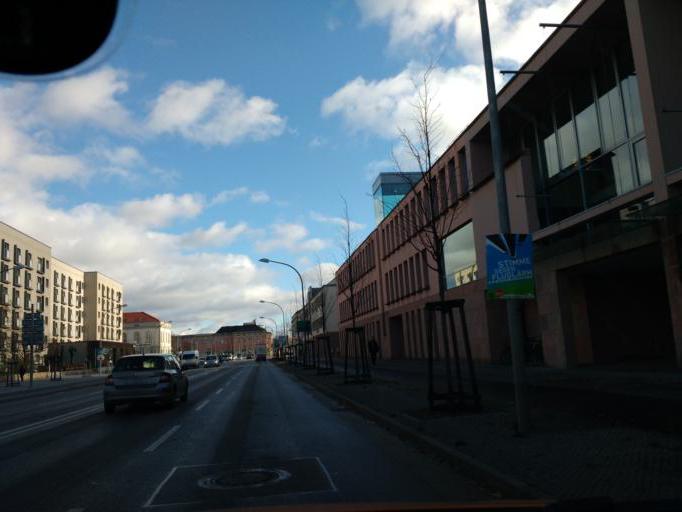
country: DE
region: Brandenburg
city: Potsdam
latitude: 52.3953
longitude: 13.0541
